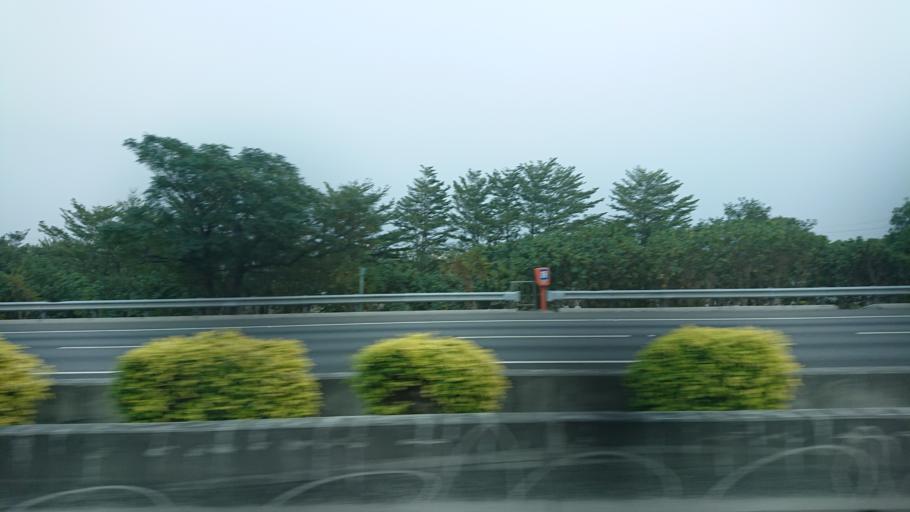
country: TW
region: Taiwan
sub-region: Nantou
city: Nantou
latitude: 23.9004
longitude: 120.4971
